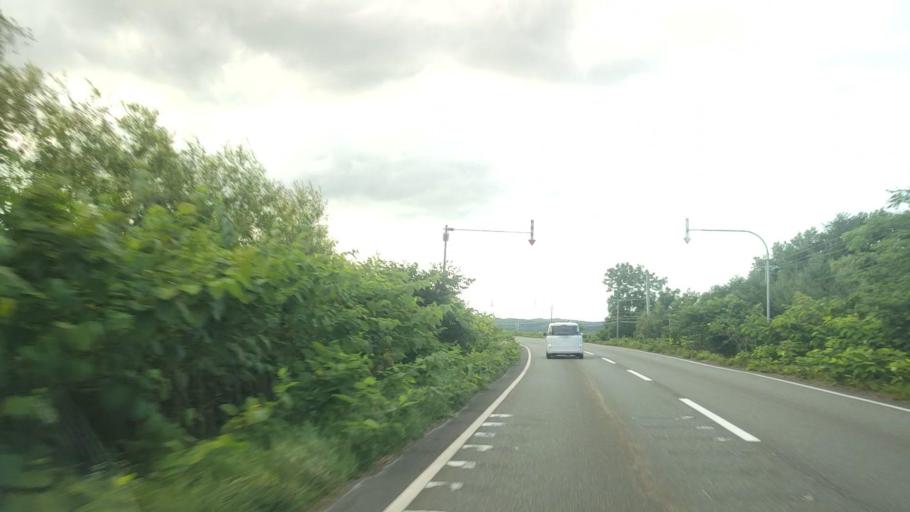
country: JP
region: Hokkaido
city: Makubetsu
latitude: 45.0031
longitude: 141.8146
